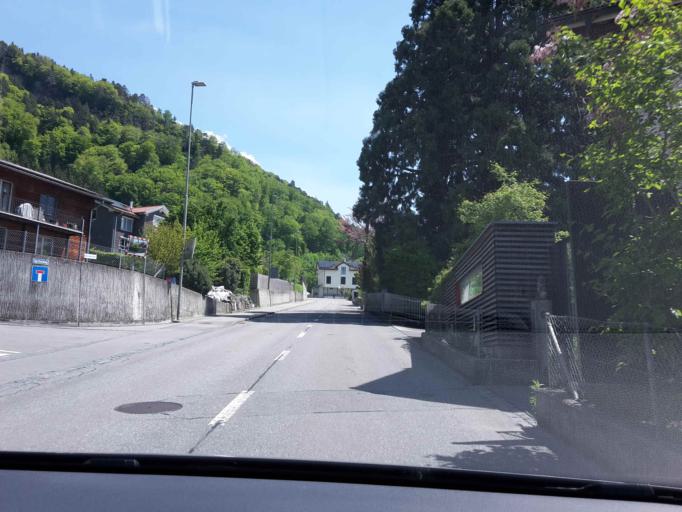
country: CH
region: Bern
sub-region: Thun District
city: Steffisburg
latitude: 46.7629
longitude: 7.6349
